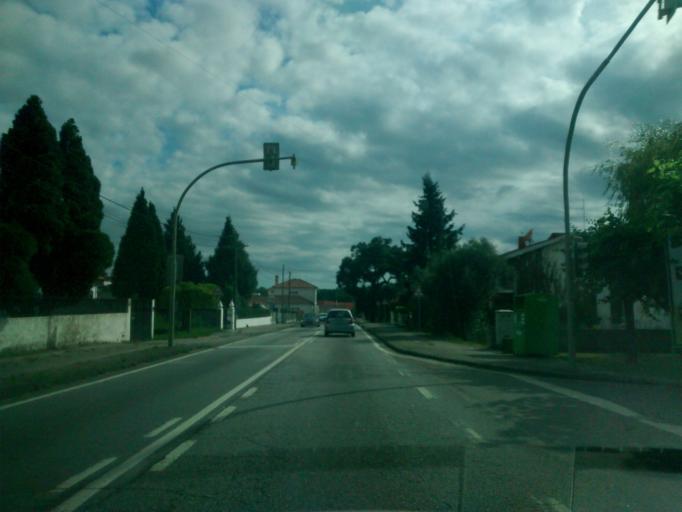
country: PT
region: Aveiro
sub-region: Anadia
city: Sangalhos
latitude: 40.4828
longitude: -8.4512
